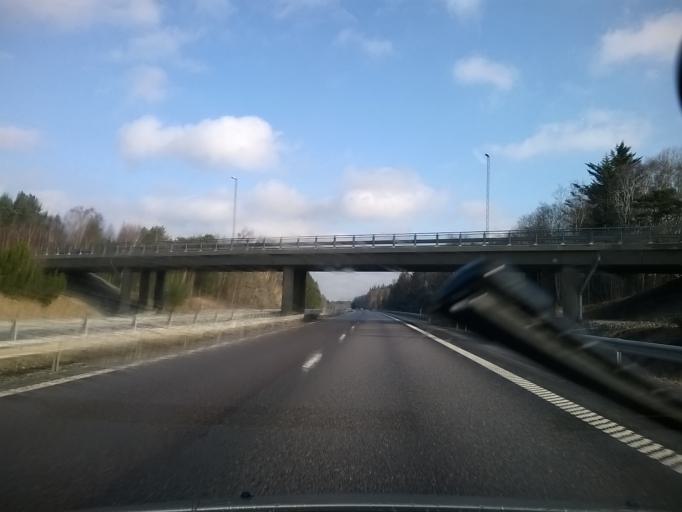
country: SE
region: Vaestra Goetaland
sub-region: Stenungsunds Kommun
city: Stora Hoga
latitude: 57.9852
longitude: 11.8421
